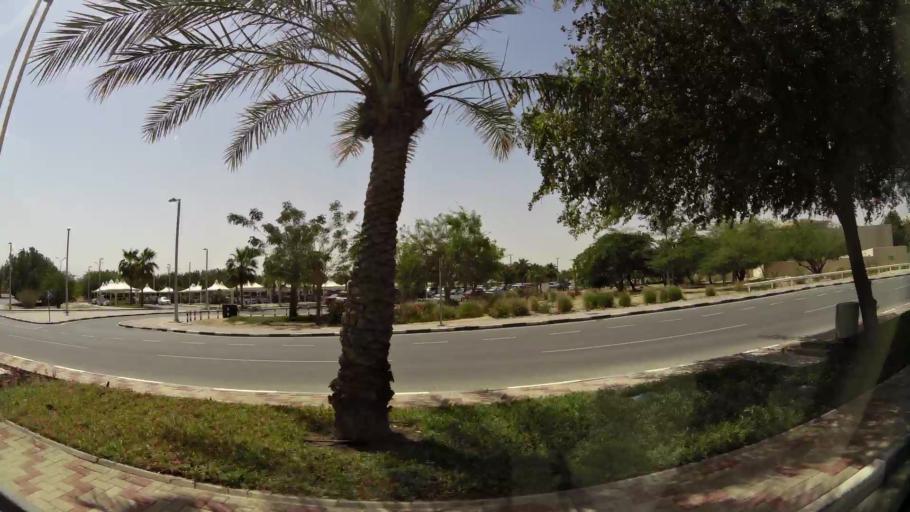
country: QA
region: Baladiyat ad Dawhah
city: Doha
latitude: 25.3738
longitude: 51.4945
